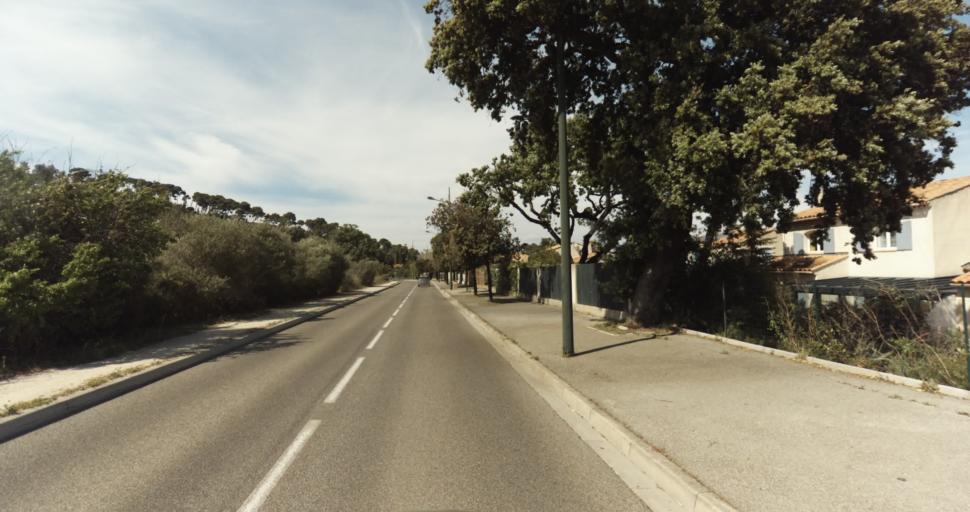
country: FR
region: Provence-Alpes-Cote d'Azur
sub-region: Departement du Var
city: Hyeres
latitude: 43.1002
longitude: 6.1213
